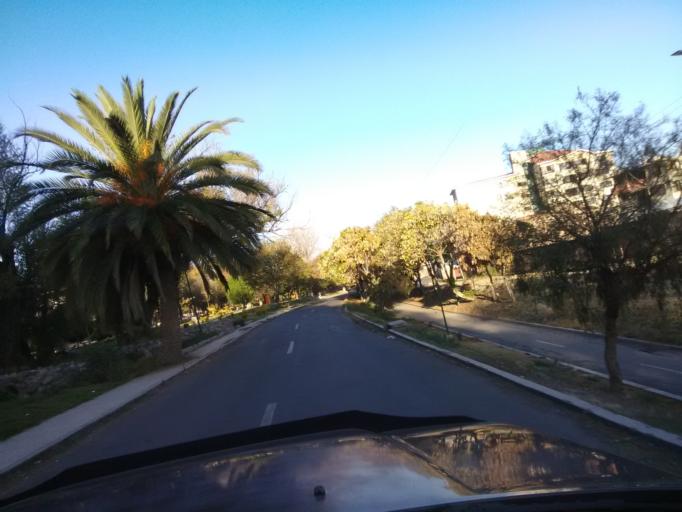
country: BO
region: Cochabamba
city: Cochabamba
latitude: -17.3654
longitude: -66.1670
